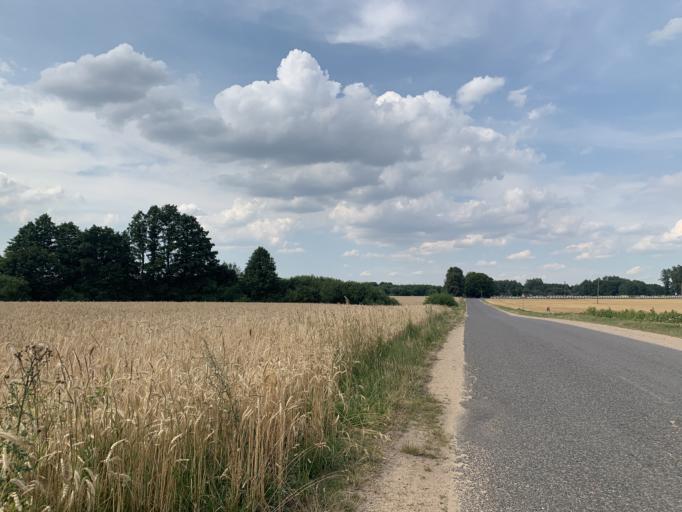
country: BY
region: Minsk
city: Nyasvizh
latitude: 53.1957
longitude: 26.6697
